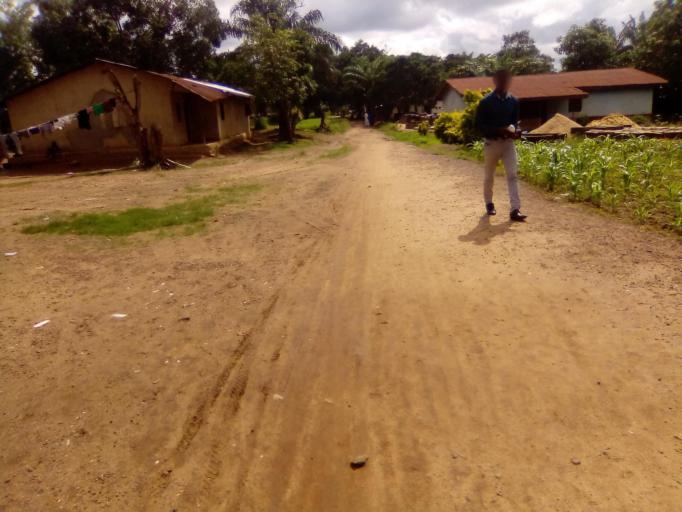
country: SL
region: Southern Province
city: Baoma
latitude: 7.9808
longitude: -11.7256
